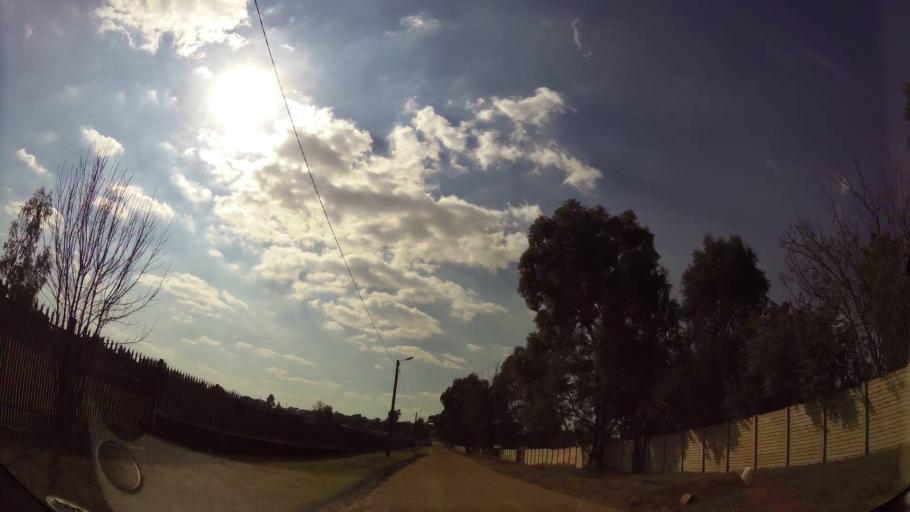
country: ZA
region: Gauteng
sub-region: Ekurhuleni Metropolitan Municipality
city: Benoni
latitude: -26.0962
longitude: 28.3498
